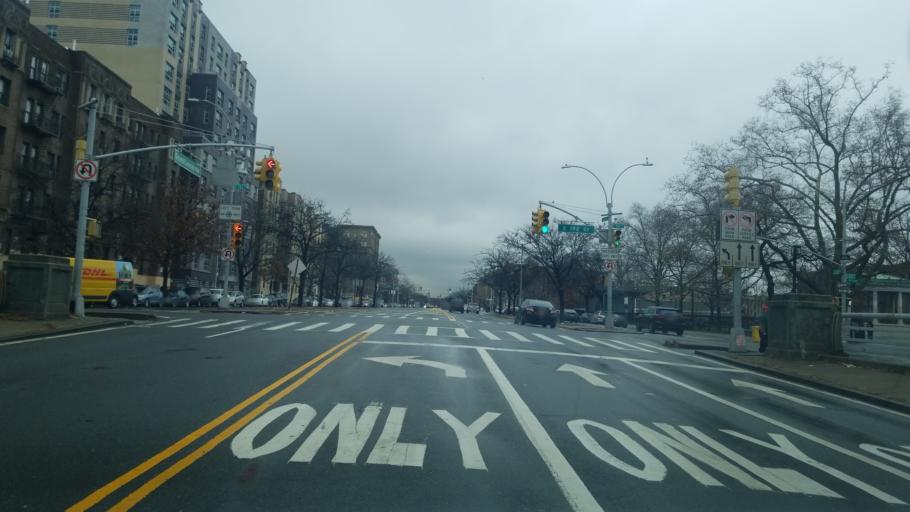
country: US
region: New York
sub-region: New York County
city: Inwood
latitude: 40.8640
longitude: -73.8960
